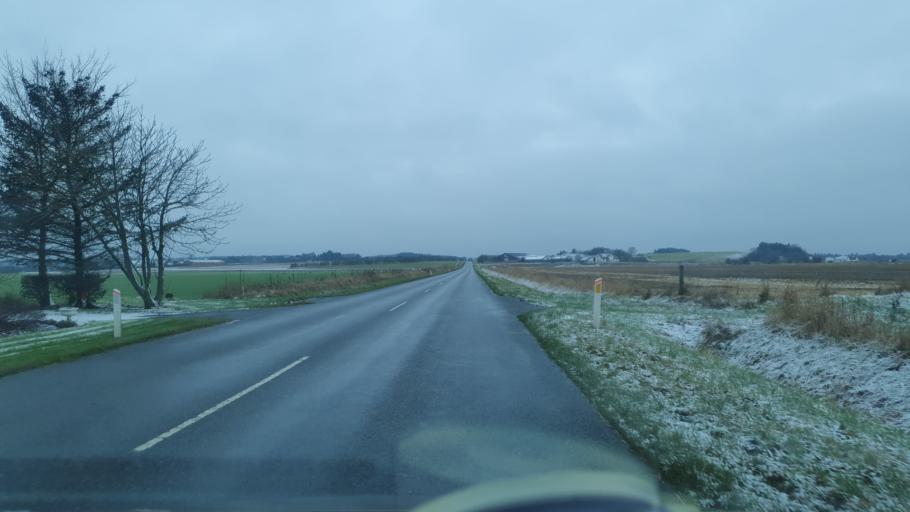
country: DK
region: North Denmark
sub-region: Jammerbugt Kommune
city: Brovst
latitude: 57.1184
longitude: 9.4974
